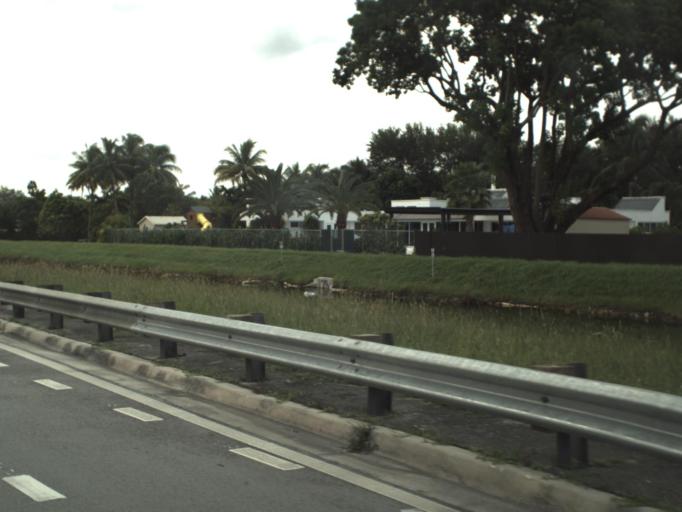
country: US
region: Florida
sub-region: Miami-Dade County
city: Tamiami
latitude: 25.7611
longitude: -80.3993
